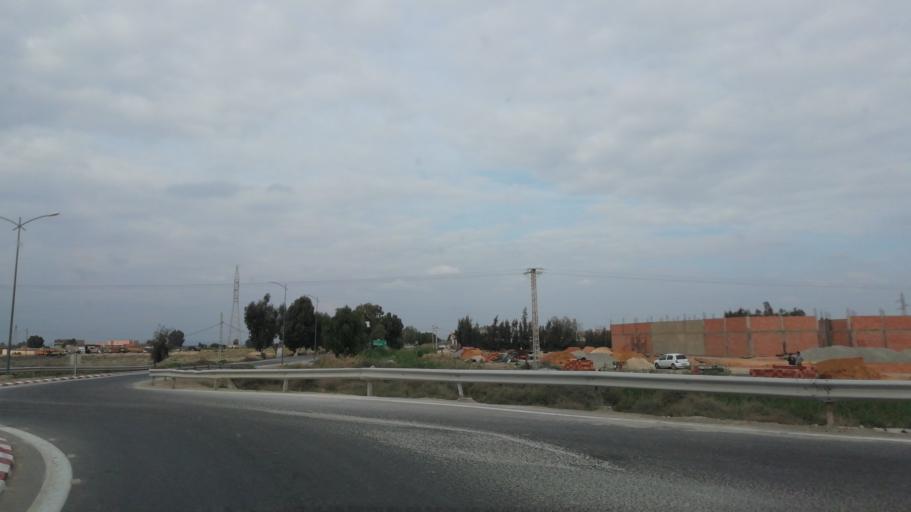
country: DZ
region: Mascara
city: Mascara
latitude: 35.6287
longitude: 0.0617
